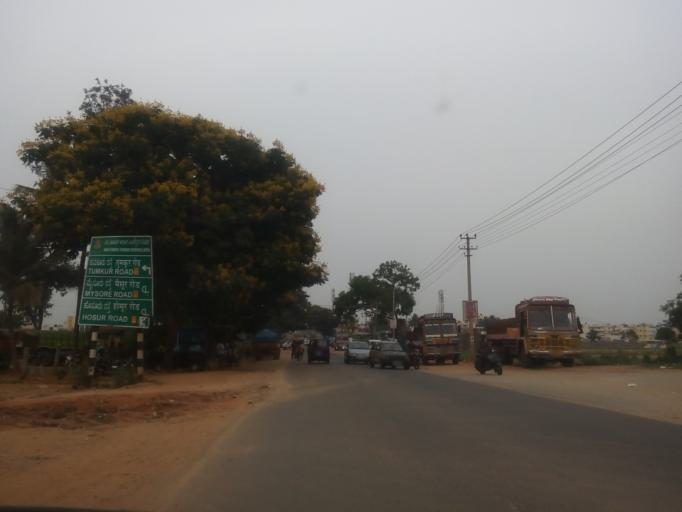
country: IN
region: Karnataka
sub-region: Bangalore Urban
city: Bangalore
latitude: 12.9898
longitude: 77.4702
